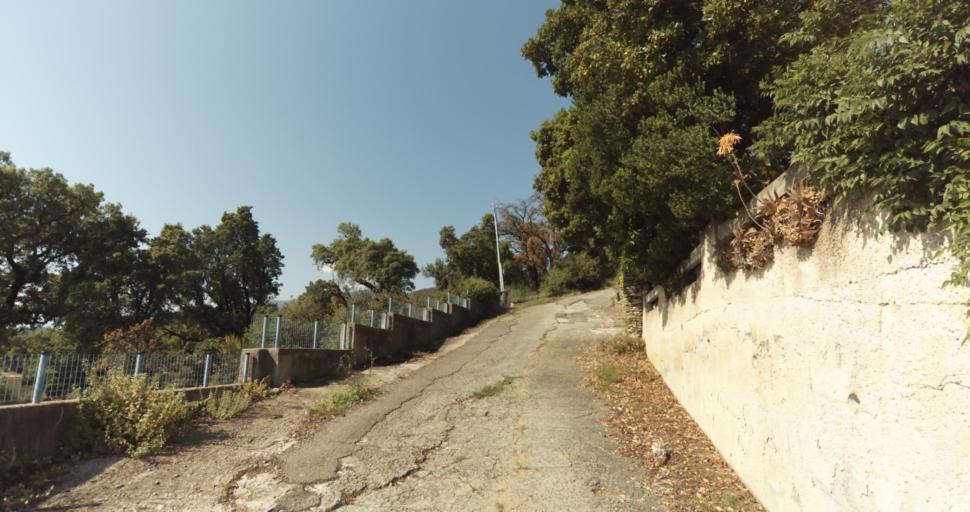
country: FR
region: Corsica
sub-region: Departement de la Haute-Corse
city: Biguglia
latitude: 42.6258
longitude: 9.4236
